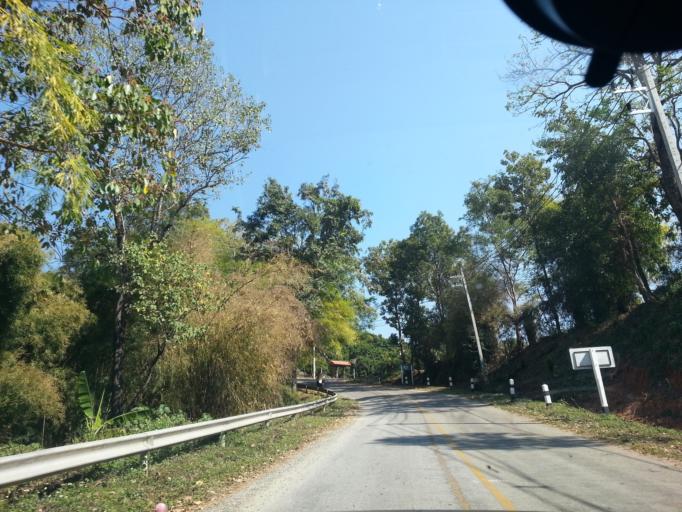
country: TH
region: Chiang Mai
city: Chai Prakan
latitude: 19.8267
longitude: 99.1005
